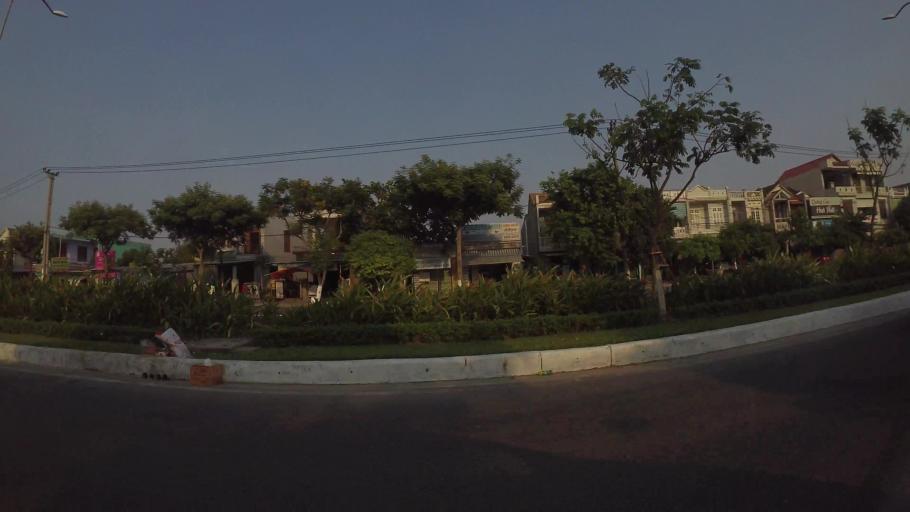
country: VN
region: Da Nang
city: Ngu Hanh Son
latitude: 15.9766
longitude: 108.2547
